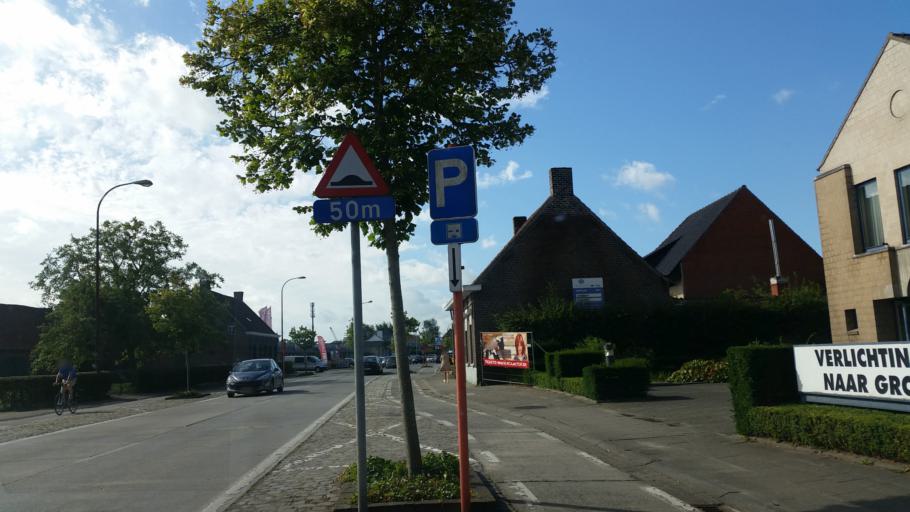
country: BE
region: Flanders
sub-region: Provincie Oost-Vlaanderen
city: Aalter
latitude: 51.0806
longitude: 3.4507
